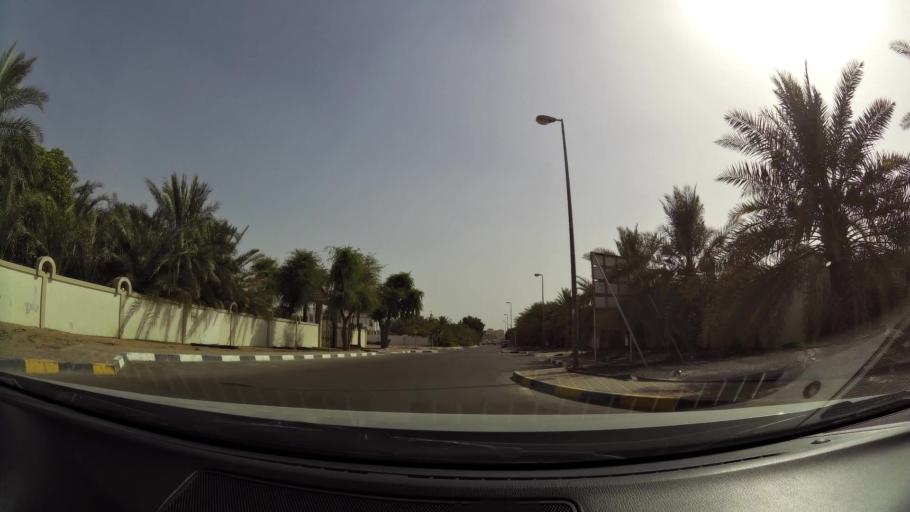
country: AE
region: Abu Dhabi
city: Al Ain
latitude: 24.2491
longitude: 55.6892
